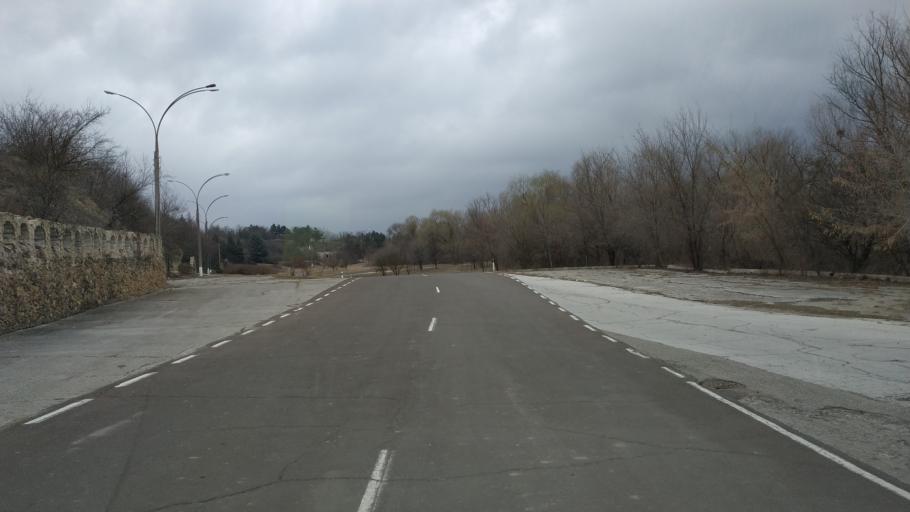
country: MD
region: Laloveni
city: Ialoveni
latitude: 46.9222
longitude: 28.8194
